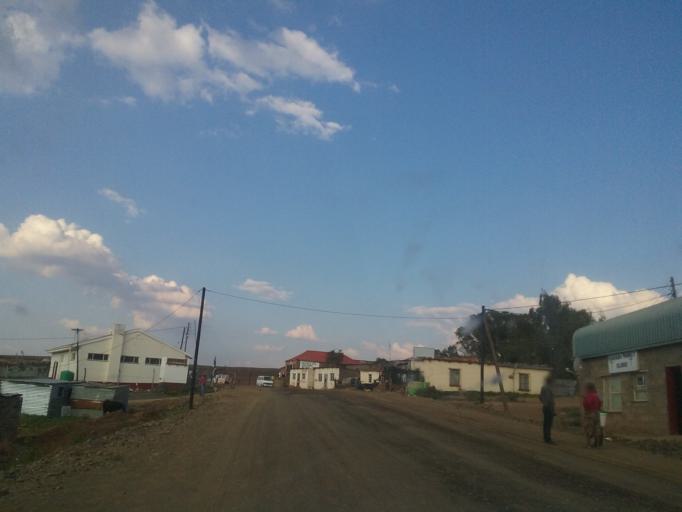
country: LS
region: Quthing
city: Quthing
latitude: -30.3950
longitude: 27.6233
